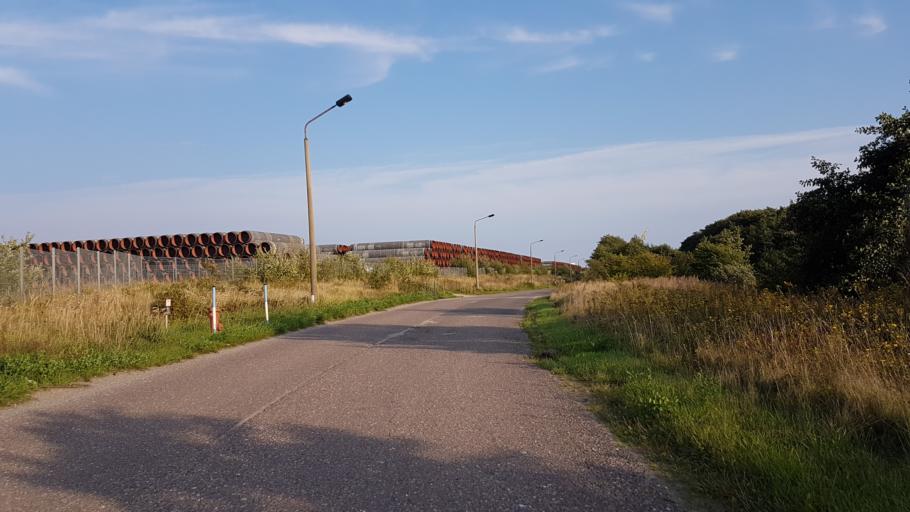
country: DE
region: Mecklenburg-Vorpommern
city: Sagard
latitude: 54.4919
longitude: 13.5689
